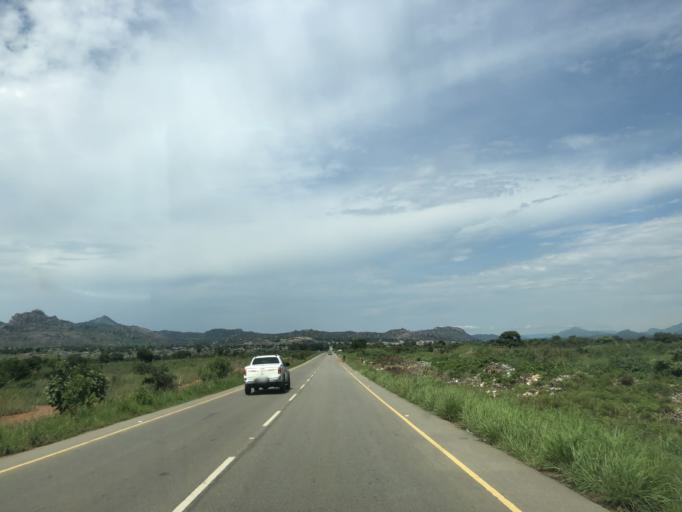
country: AO
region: Cuanza Sul
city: Quibala
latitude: -10.7344
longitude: 15.0068
